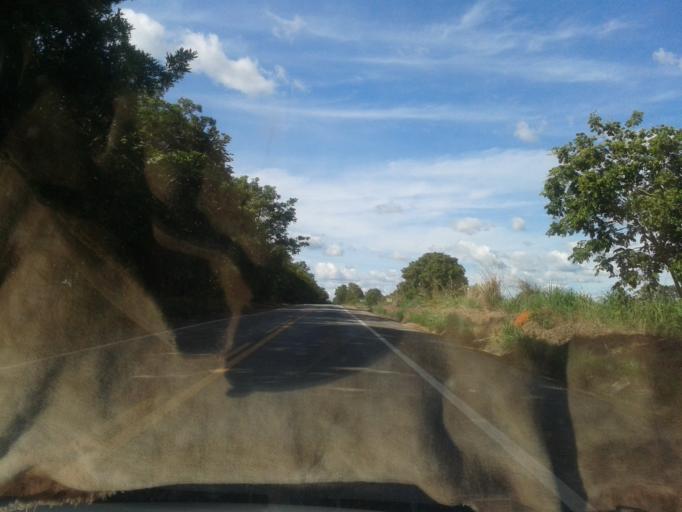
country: BR
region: Goias
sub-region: Mozarlandia
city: Mozarlandia
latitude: -14.9539
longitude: -50.5788
